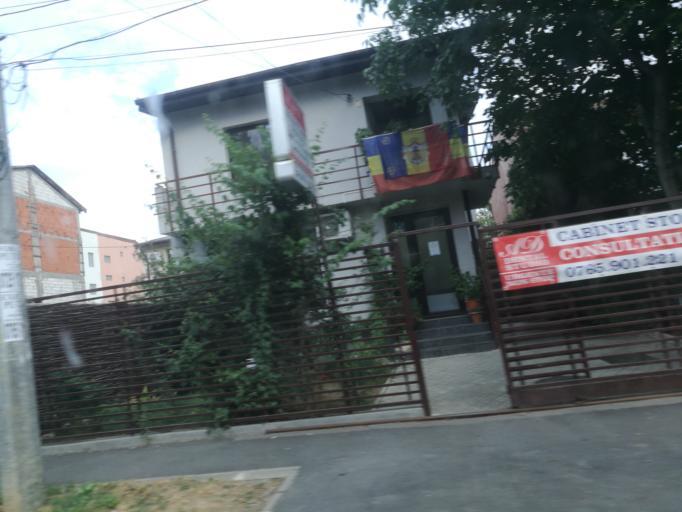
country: RO
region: Ilfov
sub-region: Comuna Chiajna
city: Rosu
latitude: 44.4882
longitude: 26.0426
